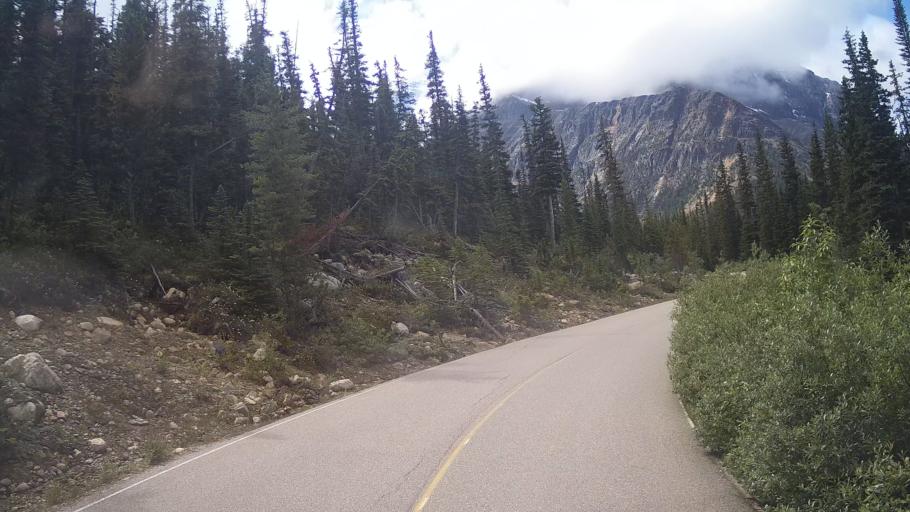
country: CA
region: Alberta
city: Jasper Park Lodge
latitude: 52.7075
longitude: -118.0576
